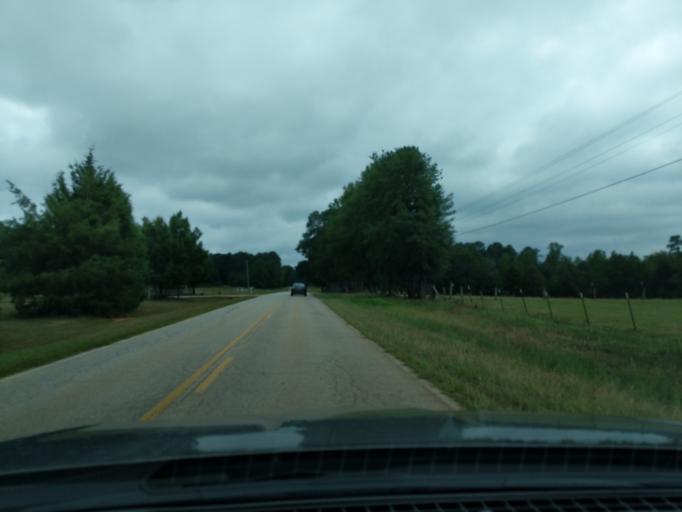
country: US
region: Georgia
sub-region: Columbia County
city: Appling
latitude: 33.6301
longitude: -82.3998
